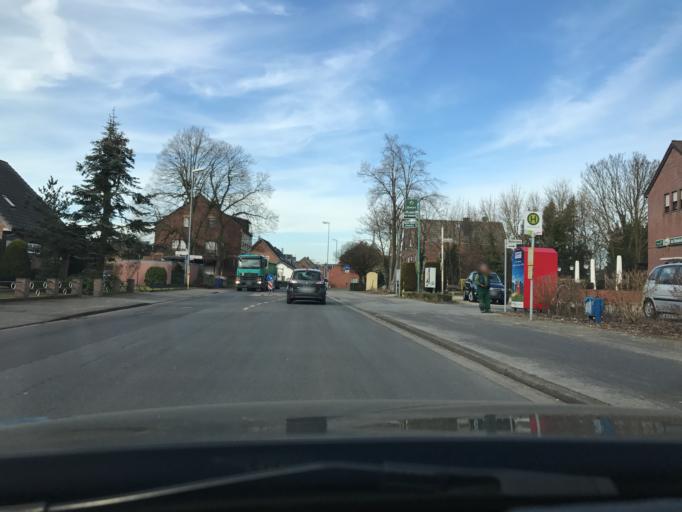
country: DE
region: North Rhine-Westphalia
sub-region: Regierungsbezirk Dusseldorf
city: Grefrath
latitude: 51.3400
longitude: 6.3685
